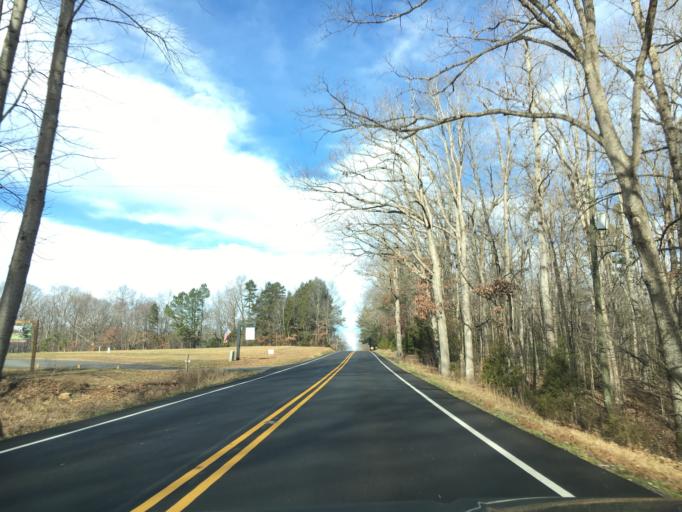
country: US
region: Virginia
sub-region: Orange County
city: Orange
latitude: 38.2551
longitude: -77.9545
